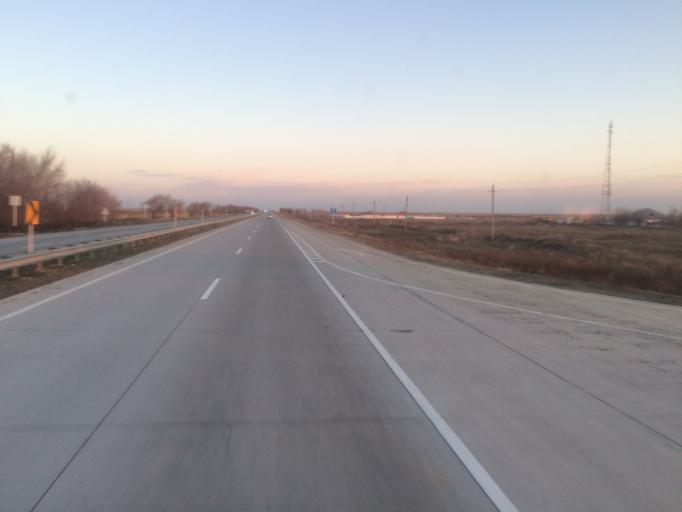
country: KZ
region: Ongtustik Qazaqstan
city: Bayaldyr
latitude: 43.0610
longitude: 68.6828
